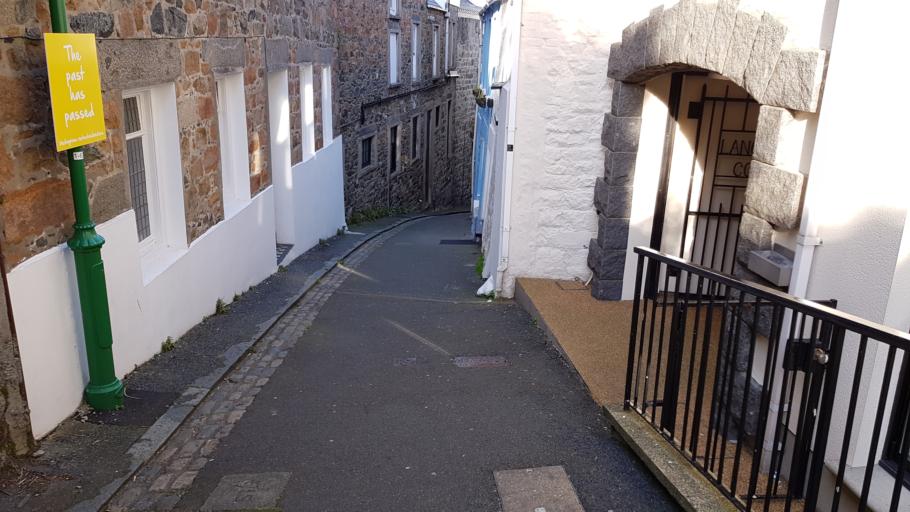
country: GG
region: St Peter Port
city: Saint Peter Port
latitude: 49.4574
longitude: -2.5365
